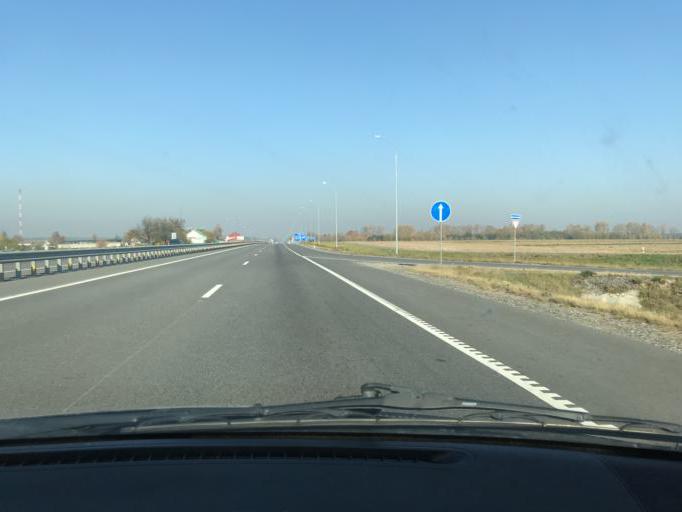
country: BY
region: Minsk
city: Slutsk
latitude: 53.2146
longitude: 27.5508
